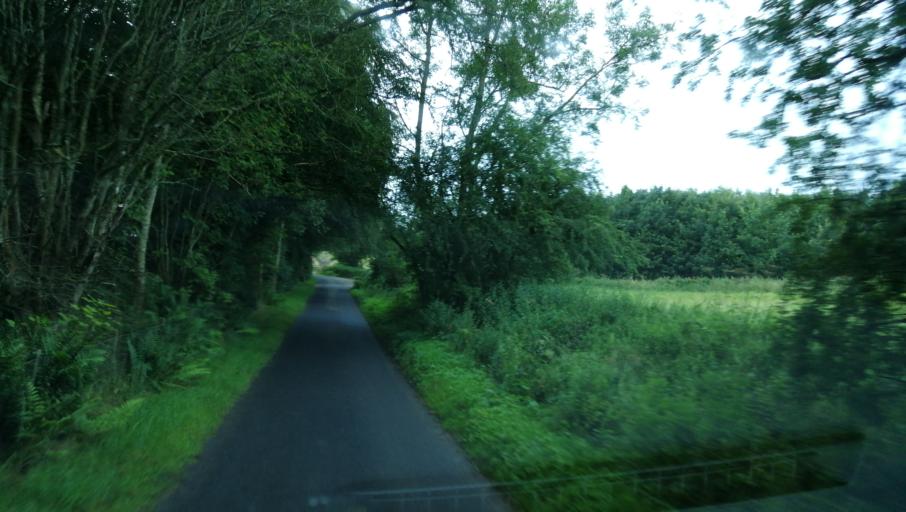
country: GB
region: Scotland
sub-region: Perth and Kinross
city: Alyth
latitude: 56.6261
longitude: -3.2803
